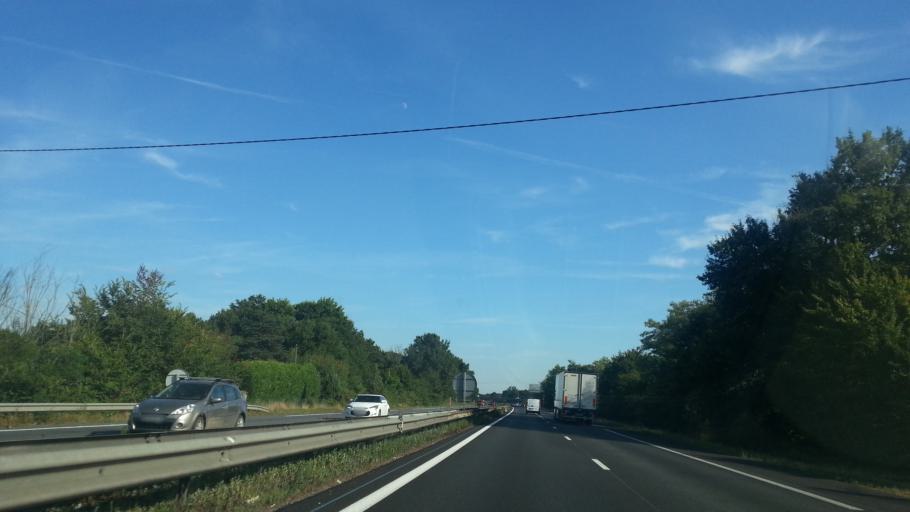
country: FR
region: Aquitaine
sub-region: Departement de la Gironde
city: Martillac
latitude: 44.7309
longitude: -0.5302
